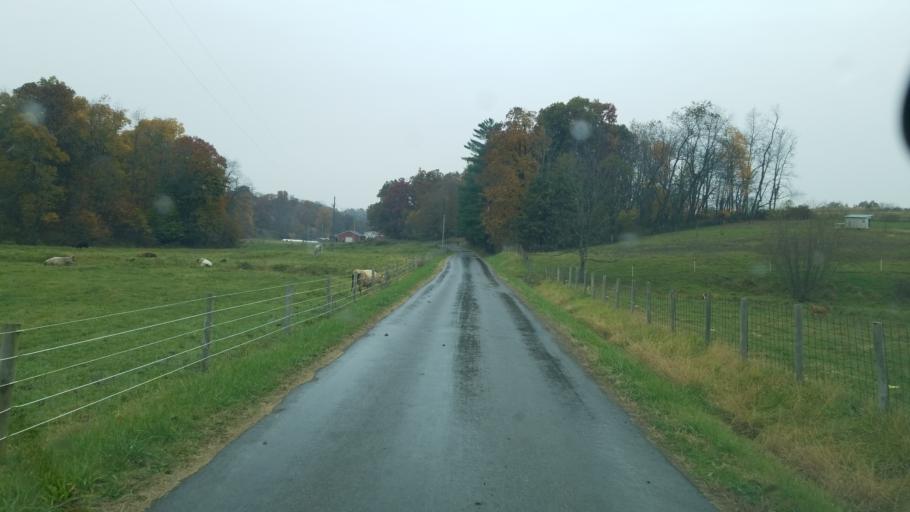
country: US
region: Ohio
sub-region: Coshocton County
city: West Lafayette
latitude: 40.4343
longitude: -81.7999
